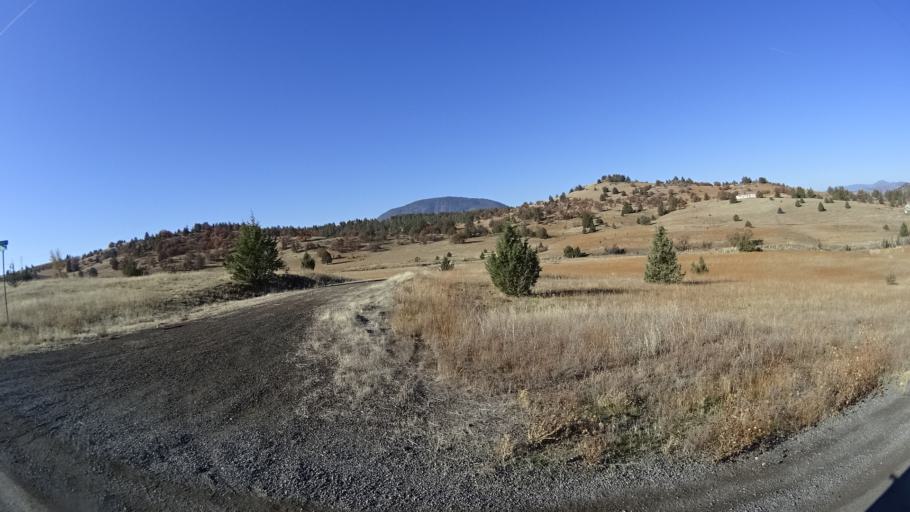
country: US
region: California
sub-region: Siskiyou County
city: Montague
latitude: 41.8795
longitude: -122.4236
